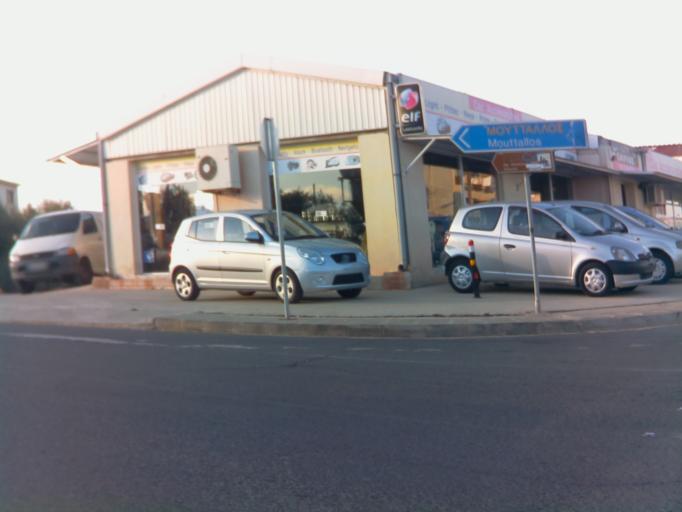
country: CY
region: Pafos
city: Paphos
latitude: 34.7833
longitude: 32.4217
